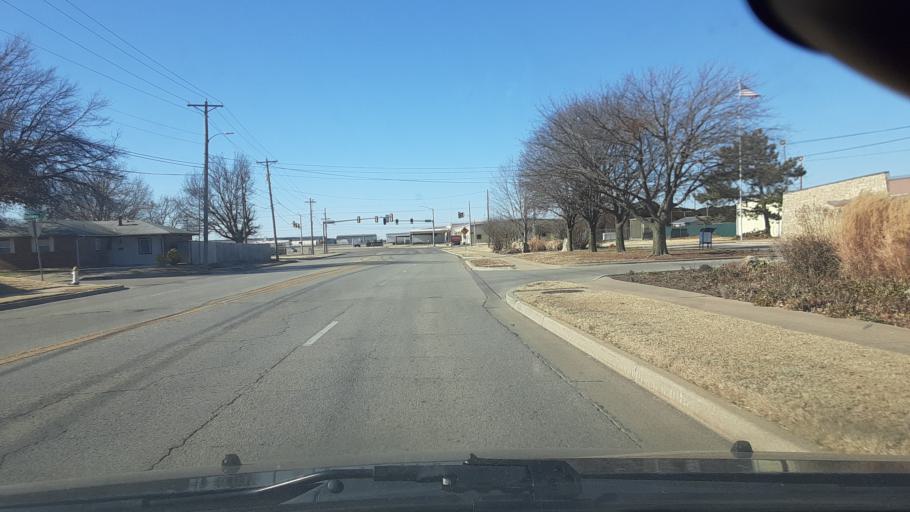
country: US
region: Oklahoma
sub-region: Kay County
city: Ponca City
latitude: 36.7243
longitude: -97.0931
